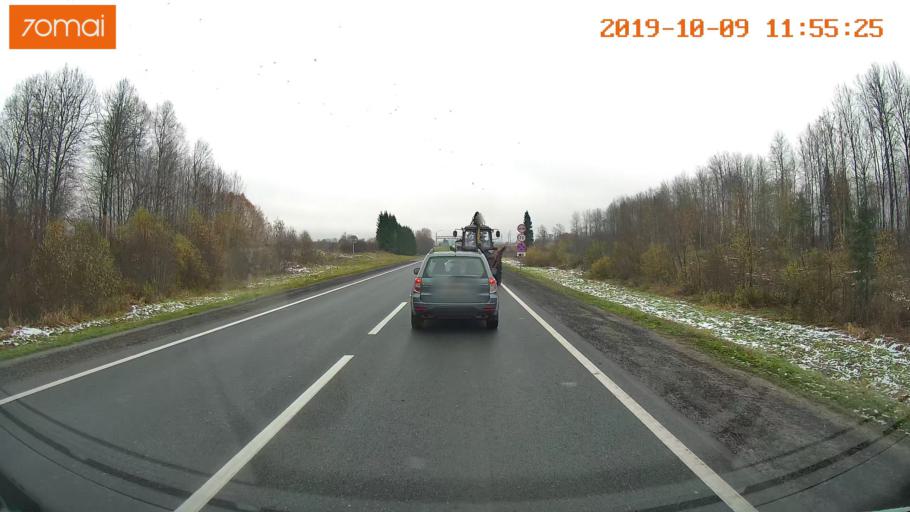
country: RU
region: Vologda
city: Gryazovets
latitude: 58.7496
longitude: 40.2853
